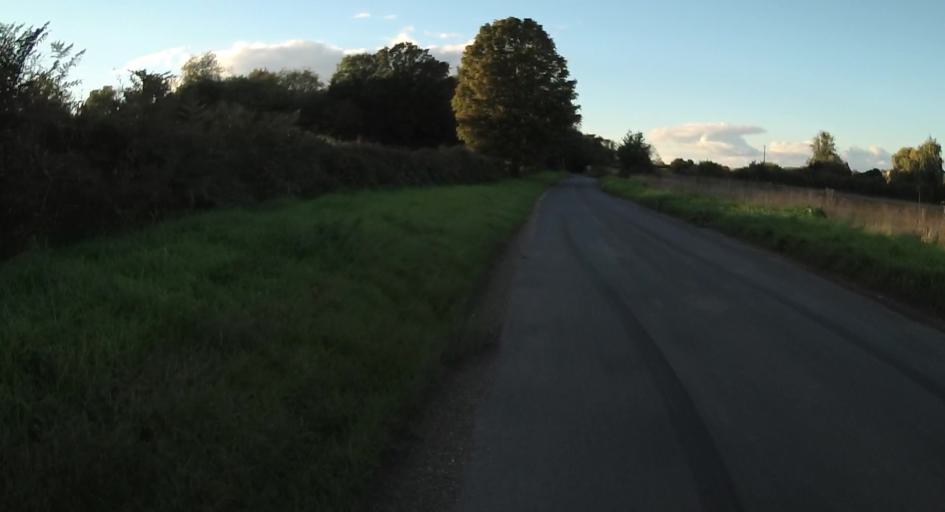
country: GB
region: England
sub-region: Hampshire
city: Odiham
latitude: 51.2380
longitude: -0.9724
